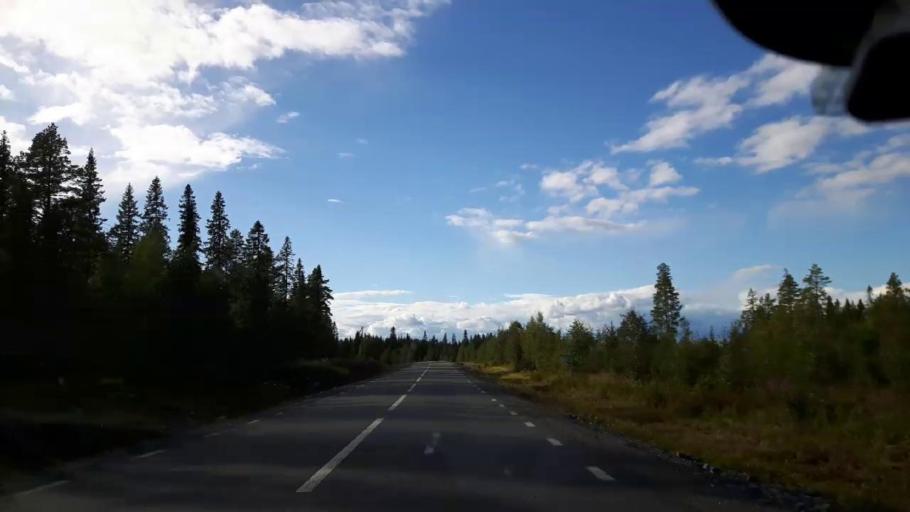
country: SE
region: Jaemtland
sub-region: Stroemsunds Kommun
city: Stroemsund
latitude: 63.5780
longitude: 15.7416
